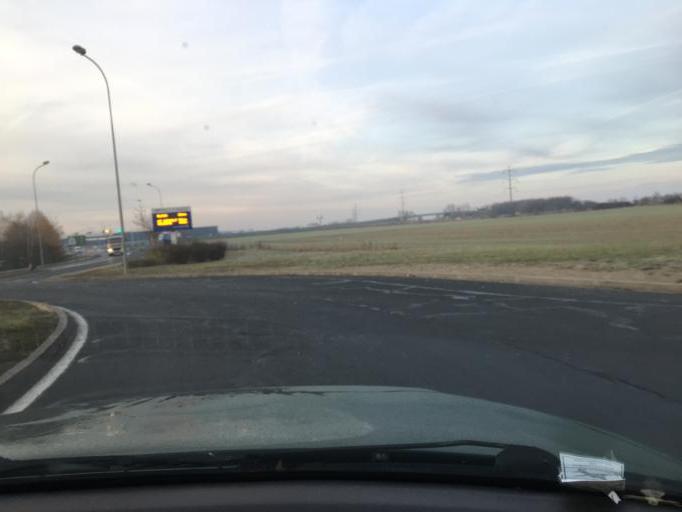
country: FR
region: Centre
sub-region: Departement du Loiret
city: Baule
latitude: 47.8344
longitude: 1.6712
